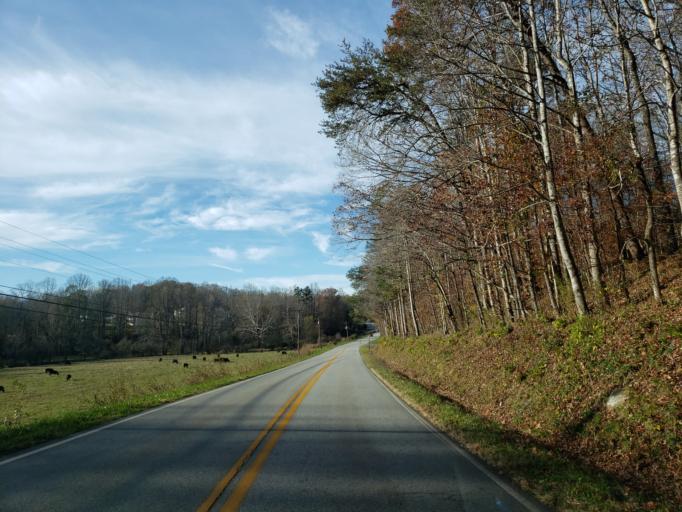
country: US
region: Georgia
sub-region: Lumpkin County
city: Dahlonega
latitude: 34.5744
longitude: -84.0152
